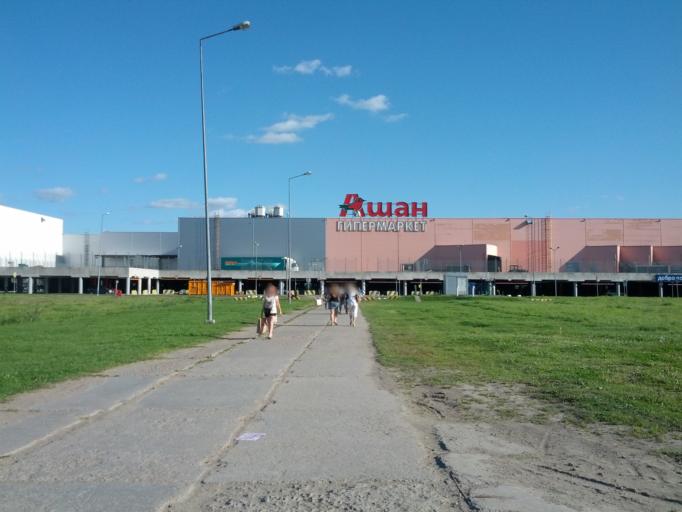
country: RU
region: Leningrad
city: Rybatskoye
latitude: 59.8965
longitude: 30.5134
